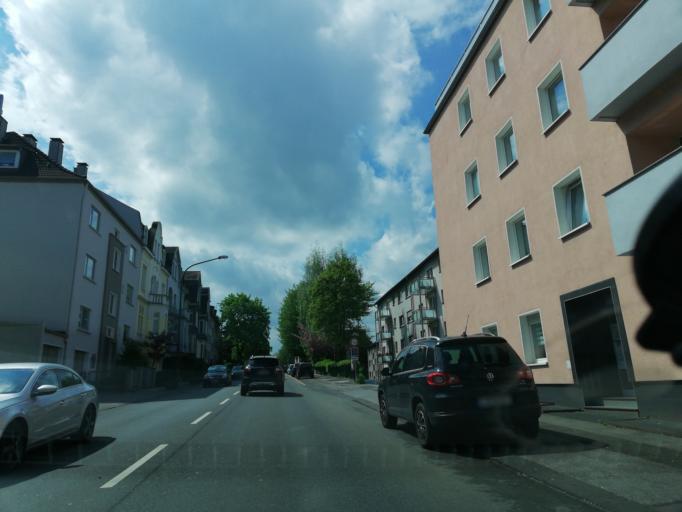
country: DE
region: North Rhine-Westphalia
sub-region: Regierungsbezirk Dusseldorf
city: Solingen
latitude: 51.2352
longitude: 7.0876
